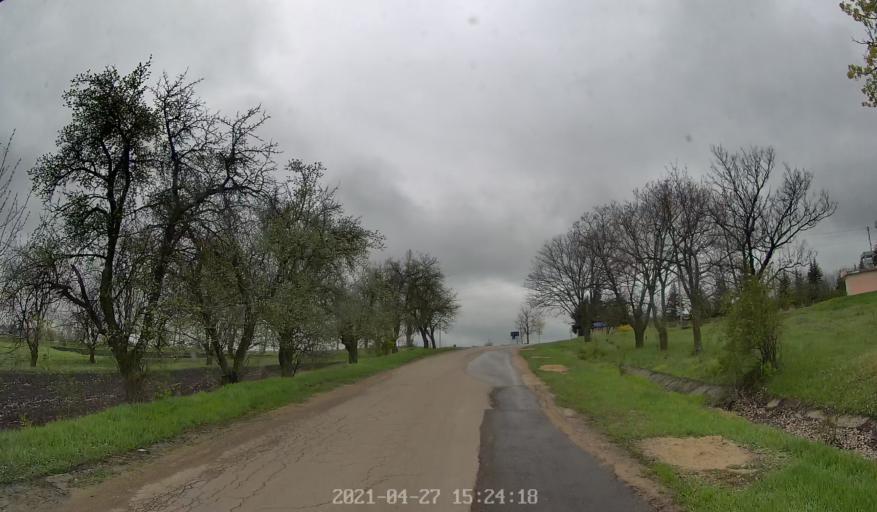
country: MD
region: Chisinau
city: Vadul lui Voda
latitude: 47.0151
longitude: 29.0243
